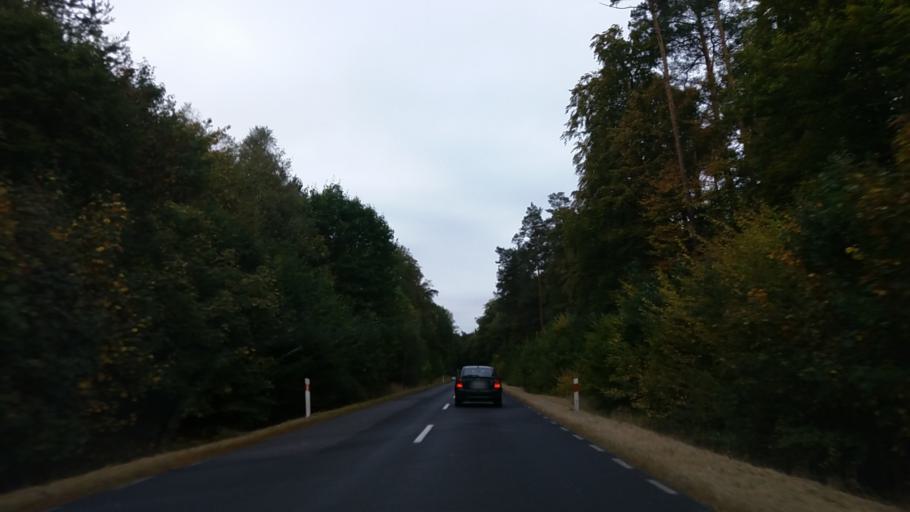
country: PL
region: Lubusz
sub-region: Powiat gorzowski
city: Klodawa
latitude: 52.8461
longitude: 15.1999
